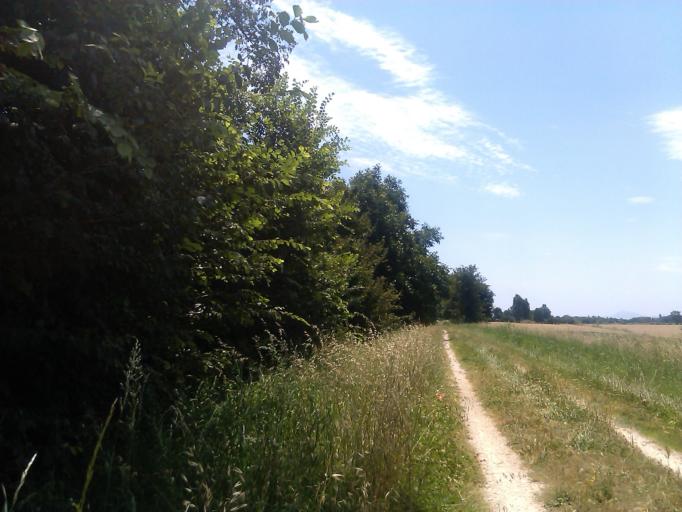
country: IT
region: Tuscany
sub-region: Province of Arezzo
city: Cesa
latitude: 43.3250
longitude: 11.8334
